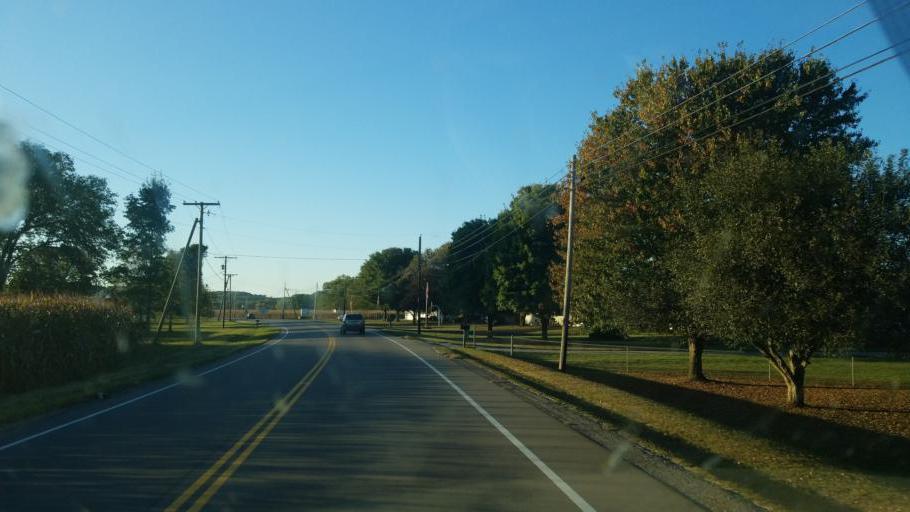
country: US
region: Ohio
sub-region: Coshocton County
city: Coshocton
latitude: 40.3299
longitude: -81.9449
